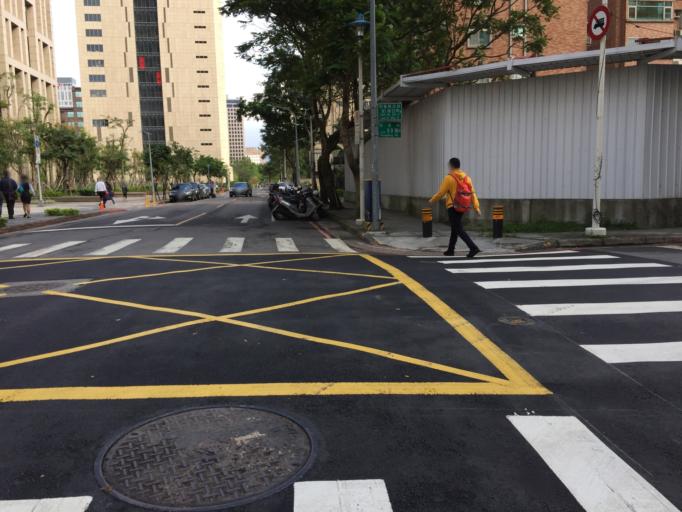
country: TW
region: Taipei
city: Taipei
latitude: 25.0336
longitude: 121.5696
